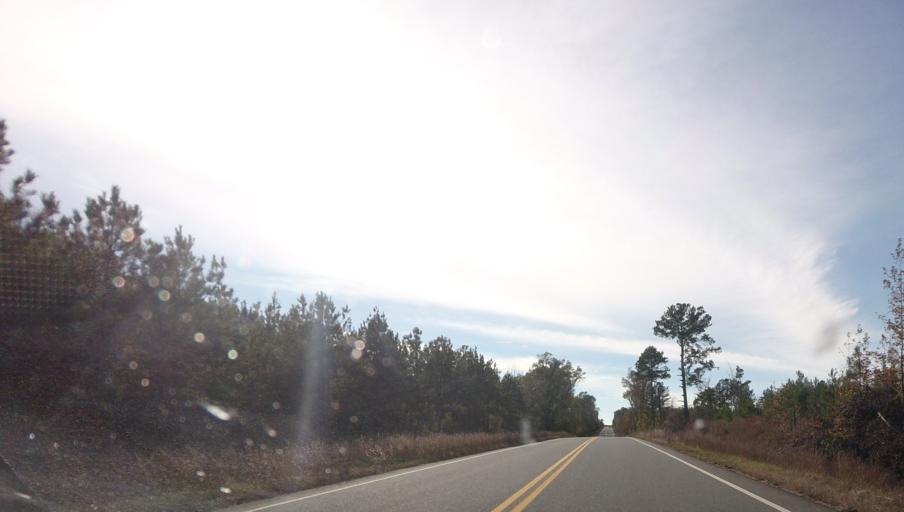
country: US
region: Georgia
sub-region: Taylor County
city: Butler
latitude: 32.7150
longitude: -84.2776
